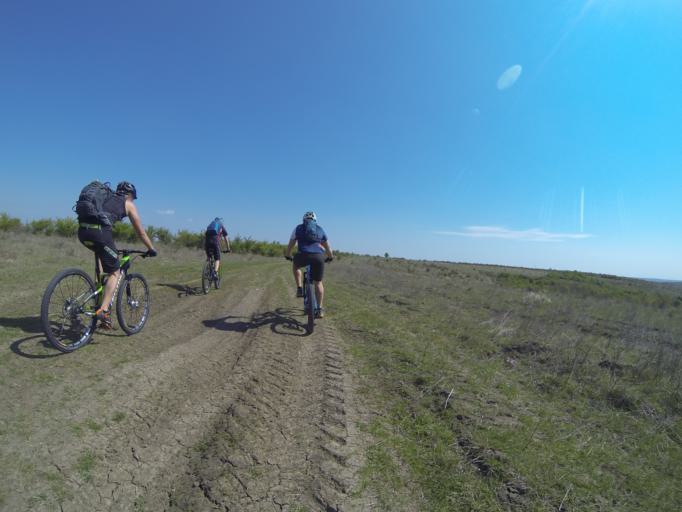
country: RO
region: Dolj
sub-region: Comuna Melinesti
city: Melinesti
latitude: 44.5506
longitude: 23.6692
